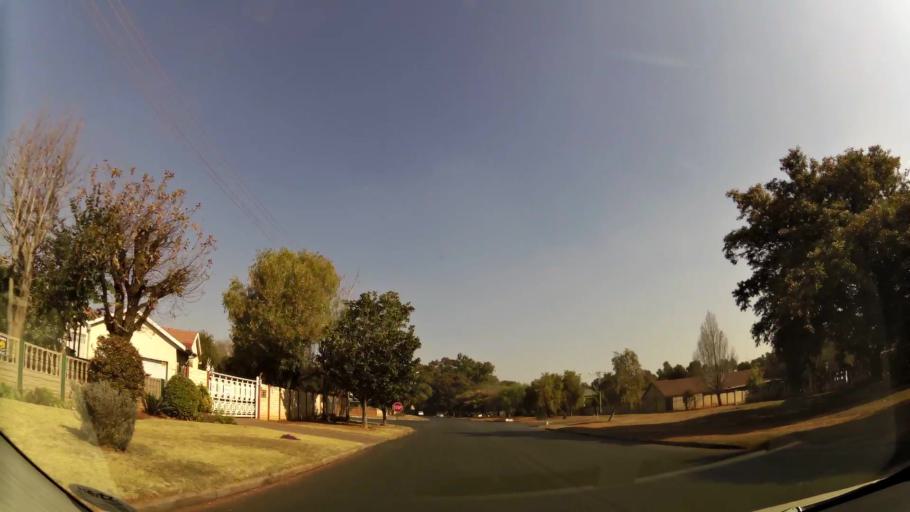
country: ZA
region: Gauteng
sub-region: West Rand District Municipality
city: Randfontein
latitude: -26.1640
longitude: 27.6898
